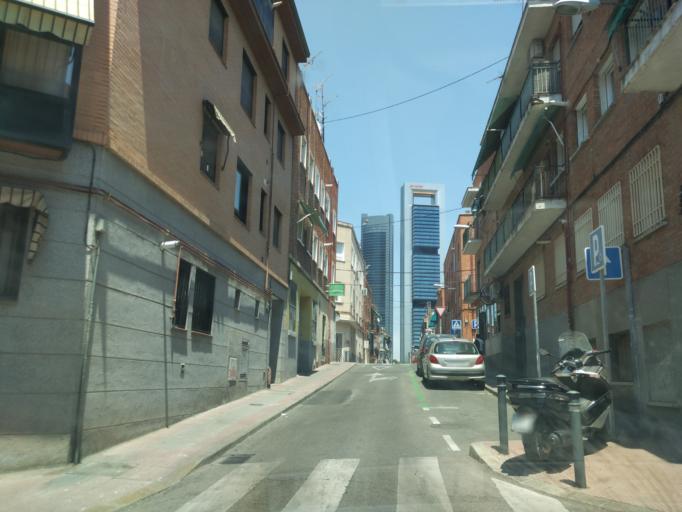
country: ES
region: Madrid
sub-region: Provincia de Madrid
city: Chamartin
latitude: 40.4694
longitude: -3.6919
